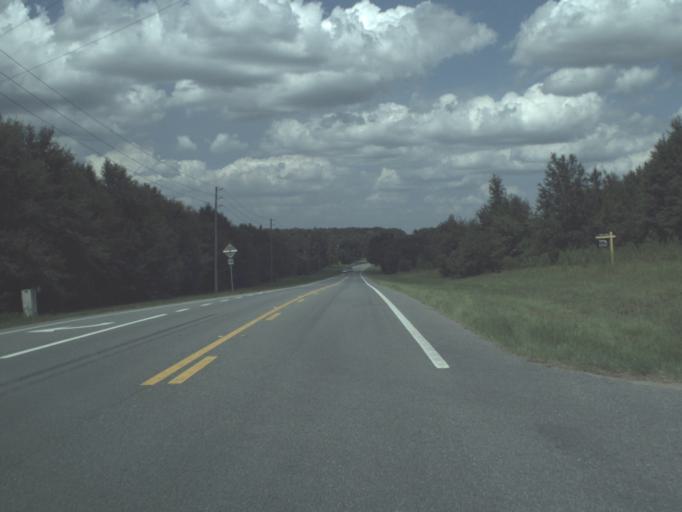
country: US
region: Florida
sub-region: Citrus County
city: Floral City
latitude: 28.7109
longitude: -82.3114
